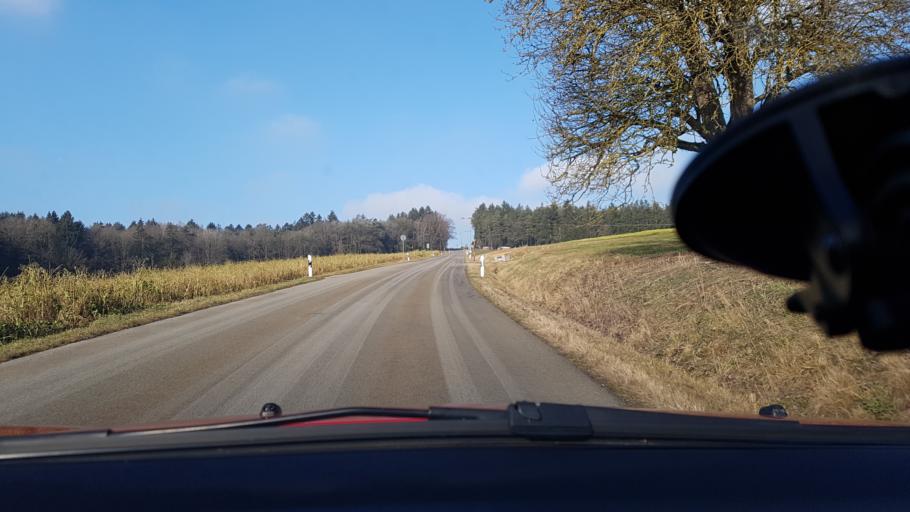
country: DE
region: Bavaria
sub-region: Lower Bavaria
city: Stubenberg
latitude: 48.3106
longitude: 13.0402
